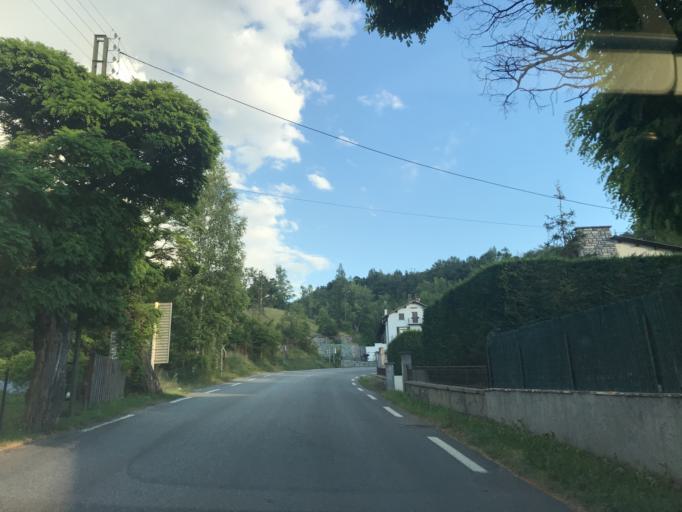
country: FR
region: Provence-Alpes-Cote d'Azur
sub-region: Departement des Hautes-Alpes
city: Guillestre
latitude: 44.6562
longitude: 6.6523
